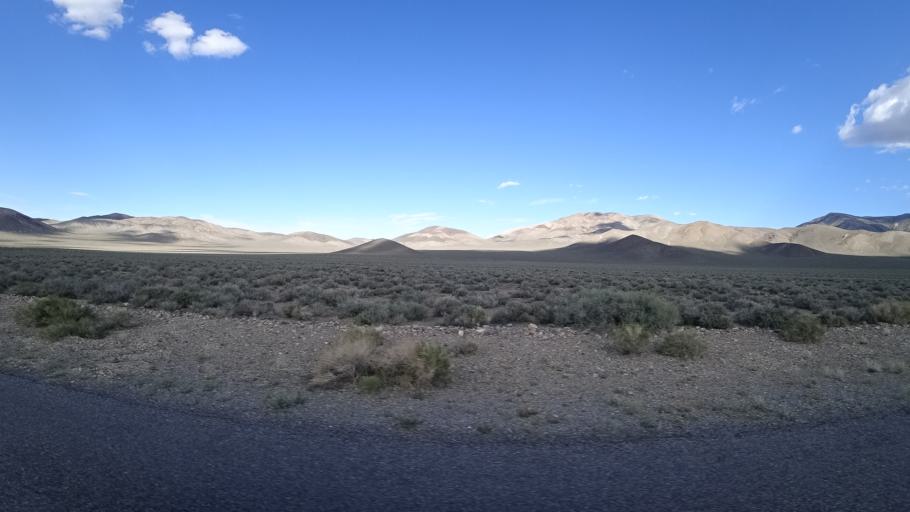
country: US
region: California
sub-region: San Bernardino County
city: Searles Valley
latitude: 36.3593
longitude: -117.1340
